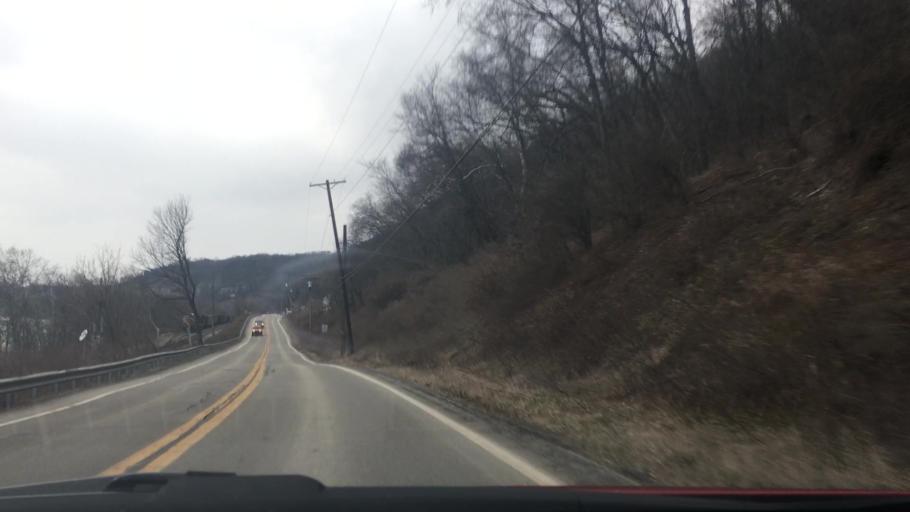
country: US
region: Pennsylvania
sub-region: Allegheny County
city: Clairton
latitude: 40.3038
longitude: -79.8675
